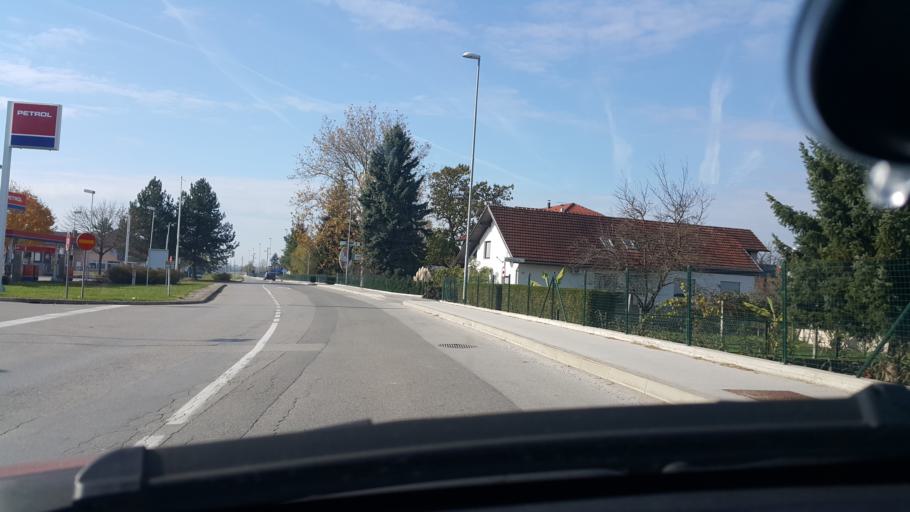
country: HR
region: Zagrebacka
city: Bregana
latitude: 45.8957
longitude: 15.6563
